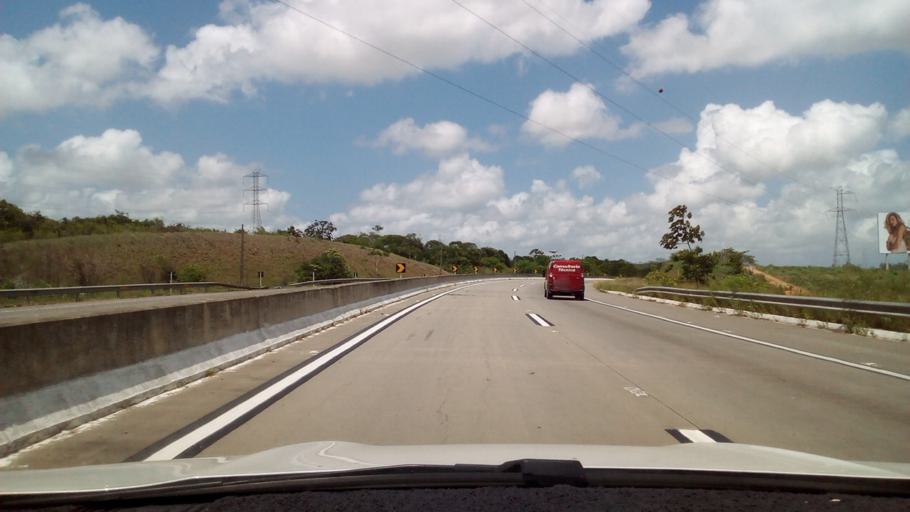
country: BR
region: Paraiba
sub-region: Conde
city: Conde
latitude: -7.3146
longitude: -34.9464
